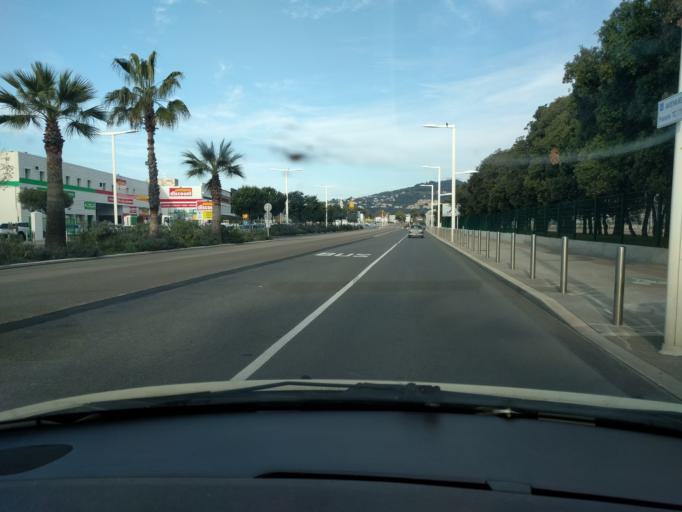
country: FR
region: Provence-Alpes-Cote d'Azur
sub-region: Departement des Alpes-Maritimes
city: Mandelieu-la-Napoule
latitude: 43.5501
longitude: 6.9649
